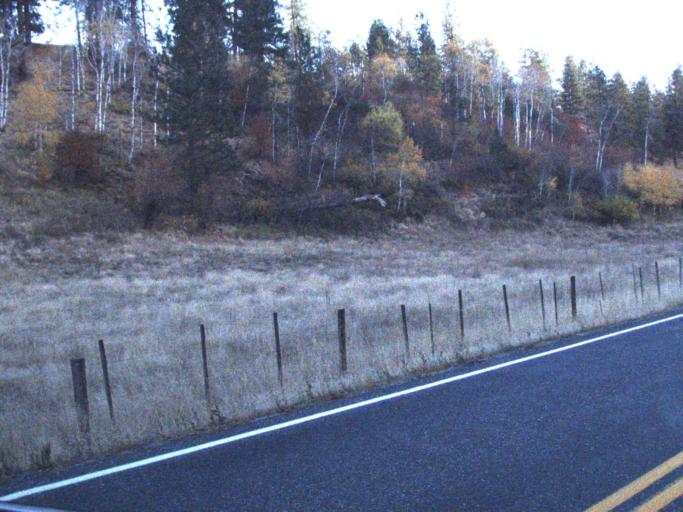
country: US
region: Washington
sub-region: Stevens County
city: Kettle Falls
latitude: 48.7328
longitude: -118.0465
